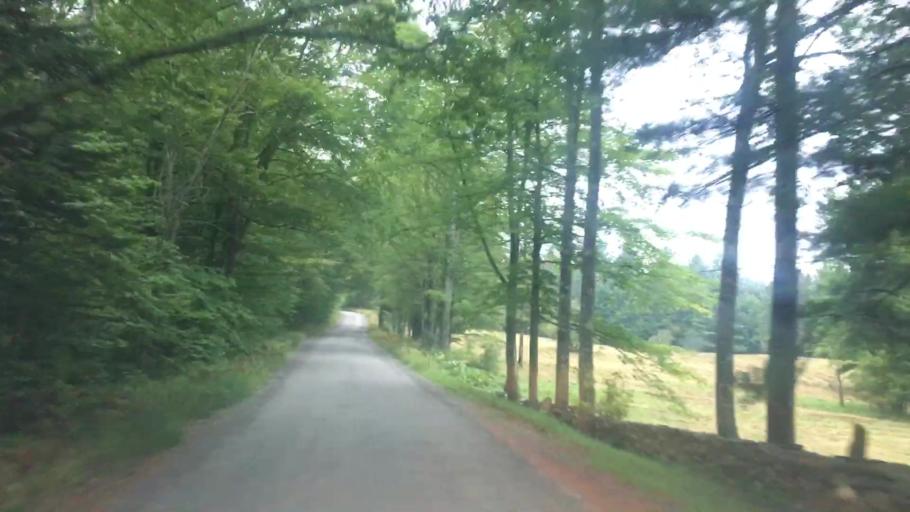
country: US
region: Vermont
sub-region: Windham County
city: Dover
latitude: 42.8431
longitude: -72.7669
